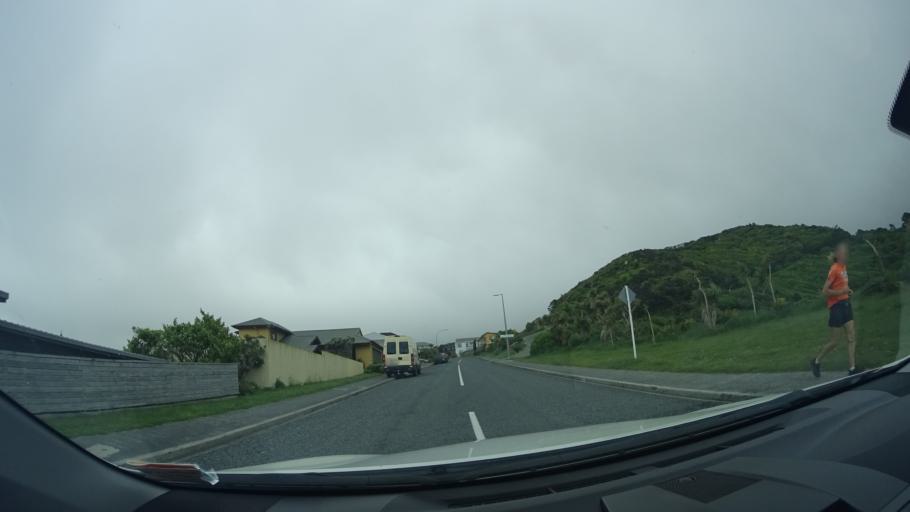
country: NZ
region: Wellington
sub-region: Wellington City
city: Brooklyn
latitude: -41.3042
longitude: 174.7542
